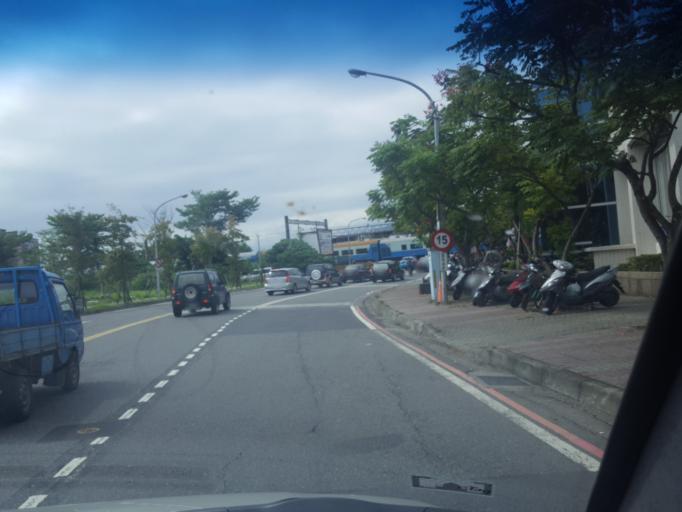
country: TW
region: Taiwan
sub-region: Yilan
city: Yilan
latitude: 24.7504
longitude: 121.7577
